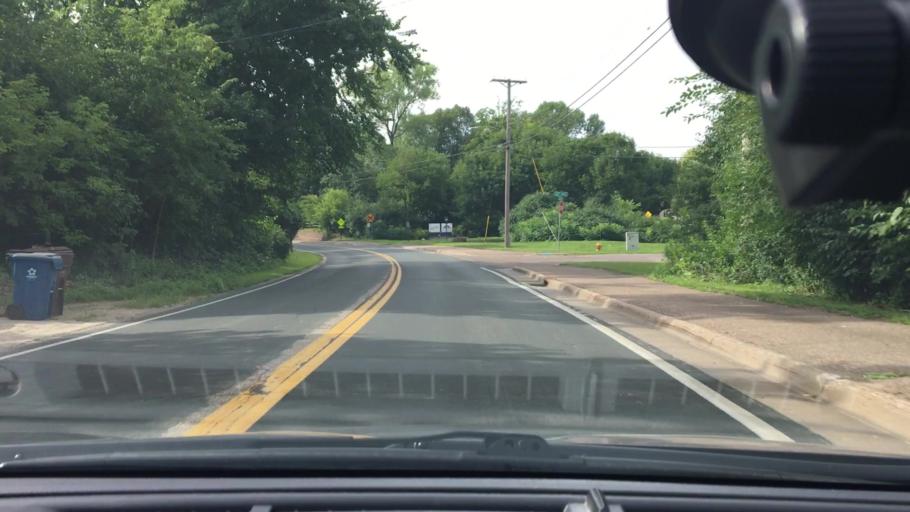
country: US
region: Minnesota
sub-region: Hennepin County
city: Plymouth
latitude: 44.9921
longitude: -93.4249
